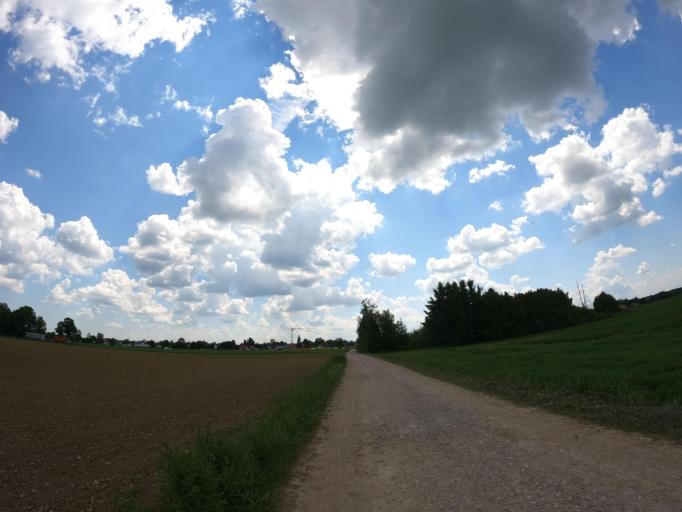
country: DE
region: Bavaria
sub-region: Upper Bavaria
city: Sauerlach
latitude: 47.9828
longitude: 11.6453
